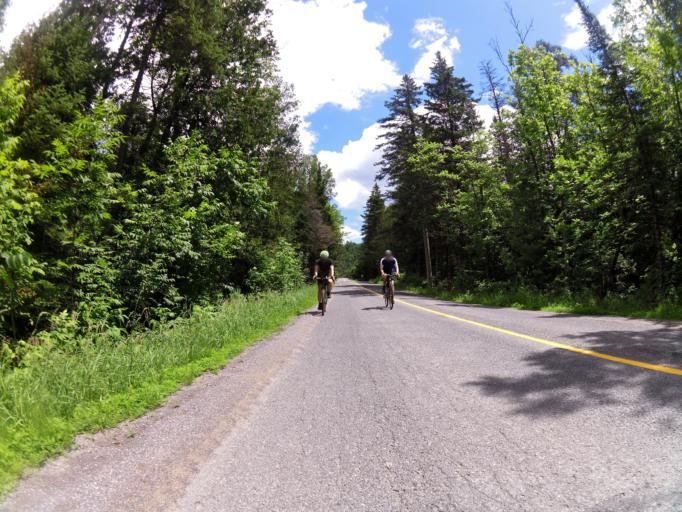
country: CA
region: Ontario
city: Renfrew
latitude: 45.0418
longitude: -76.7055
